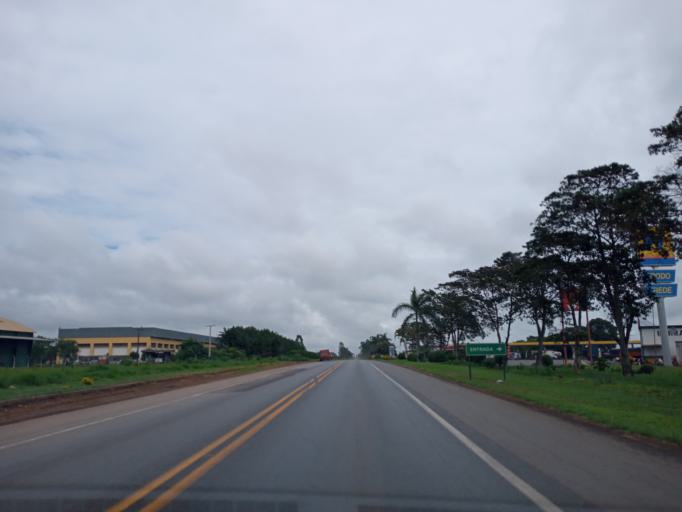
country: BR
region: Minas Gerais
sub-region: Campos Altos
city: Campos Altos
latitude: -19.6585
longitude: -46.2110
